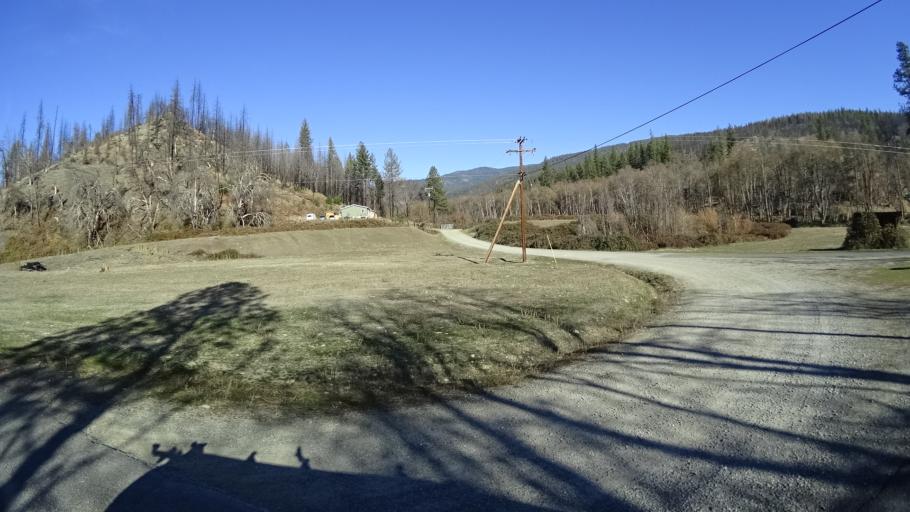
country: US
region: California
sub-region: Siskiyou County
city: Happy Camp
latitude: 41.8424
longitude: -123.0281
